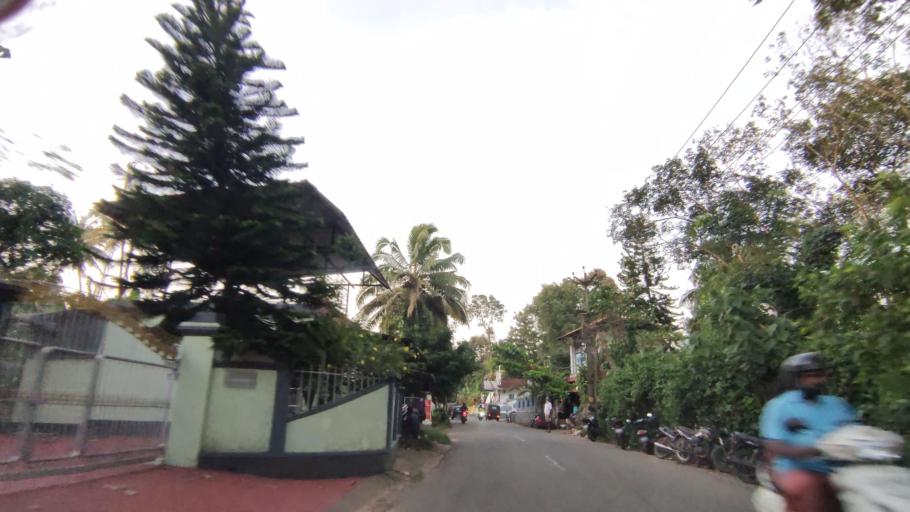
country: IN
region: Kerala
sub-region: Kottayam
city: Kottayam
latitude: 9.6605
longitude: 76.5069
